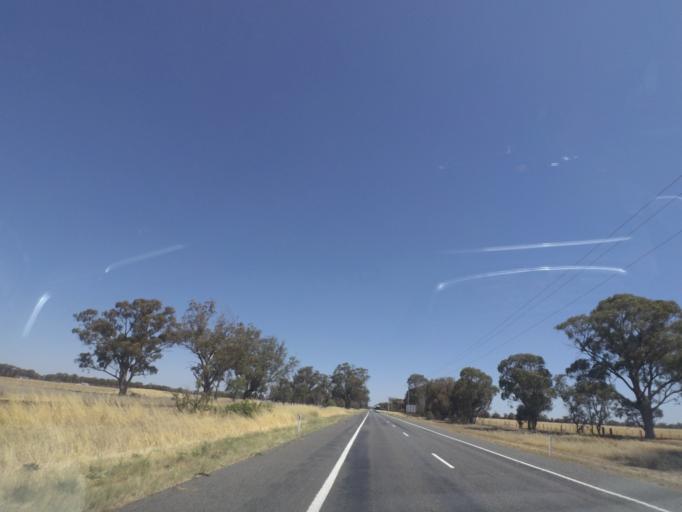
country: AU
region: Victoria
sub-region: Greater Shepparton
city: Shepparton
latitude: -36.2060
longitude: 145.4319
